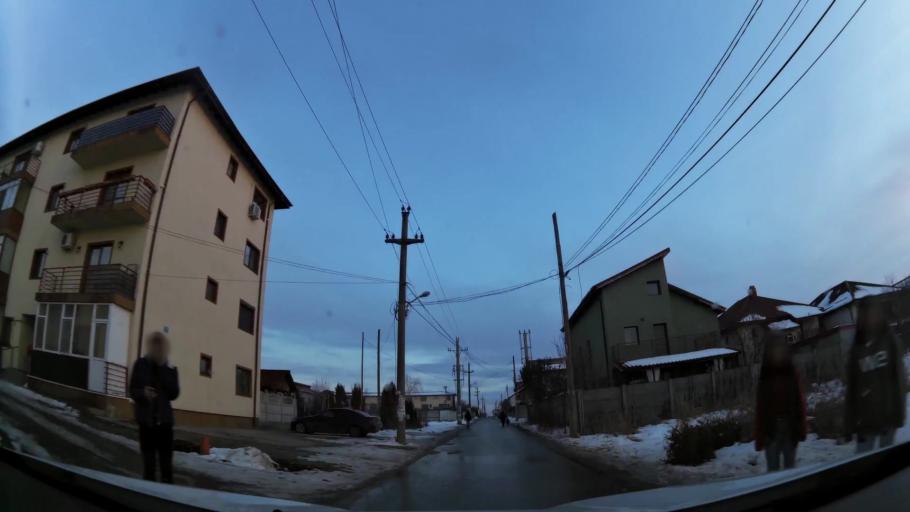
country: RO
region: Ilfov
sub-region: Comuna Magurele
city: Magurele
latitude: 44.3872
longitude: 26.0218
